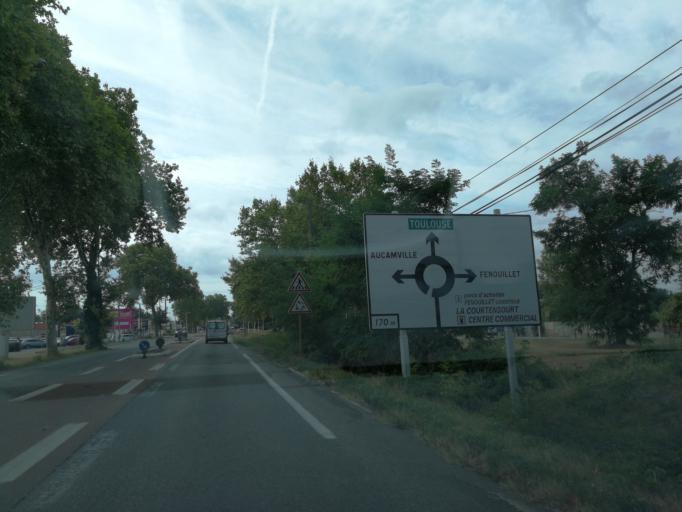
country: FR
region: Midi-Pyrenees
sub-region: Departement de la Haute-Garonne
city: Saint-Alban
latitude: 43.6787
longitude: 1.4079
